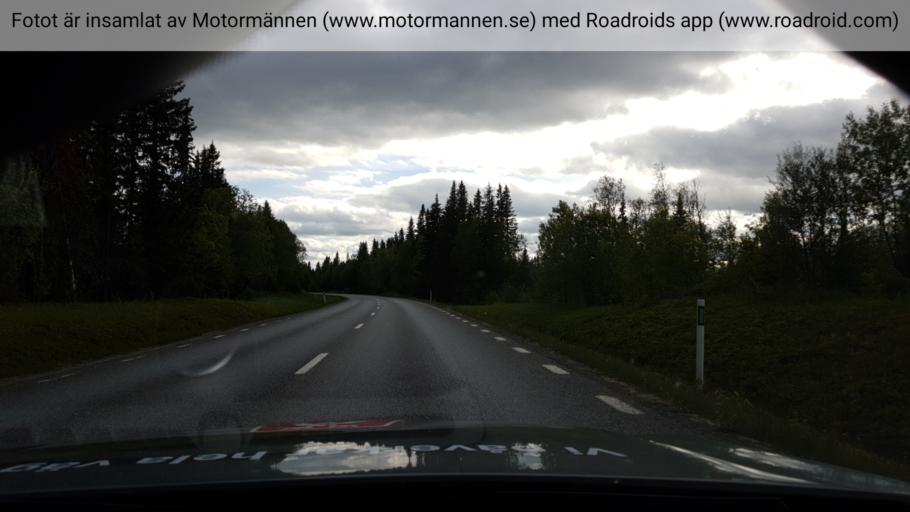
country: SE
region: Jaemtland
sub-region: OEstersunds Kommun
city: Lit
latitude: 63.4397
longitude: 15.1304
